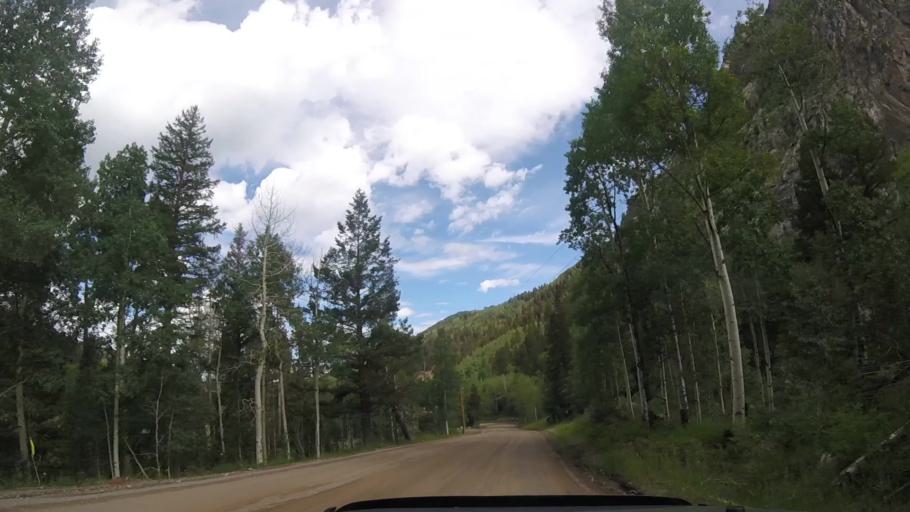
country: US
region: Colorado
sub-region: San Miguel County
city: Mountain Village
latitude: 37.8594
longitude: -107.8682
